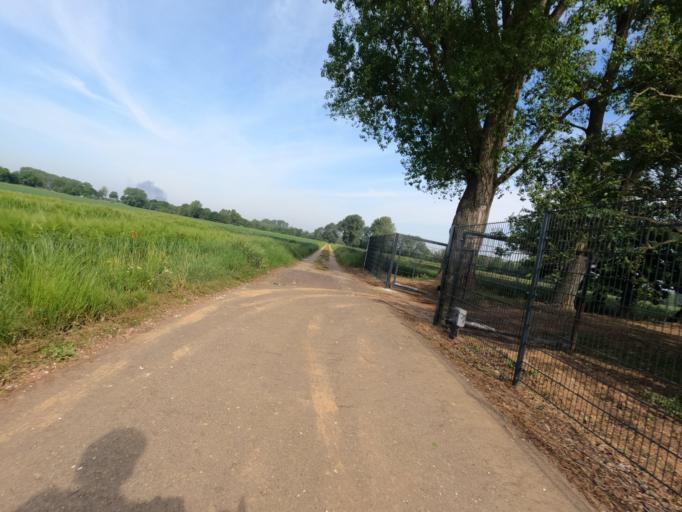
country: DE
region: North Rhine-Westphalia
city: Huckelhoven
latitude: 51.0475
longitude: 6.2011
